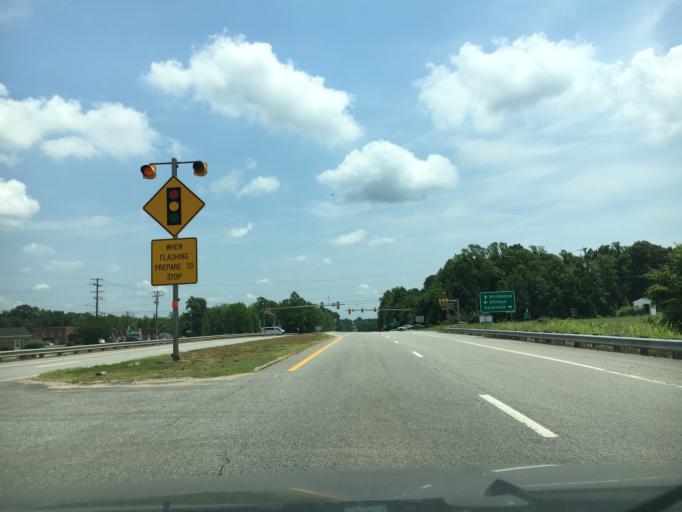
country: US
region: Virginia
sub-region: Buckingham County
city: Buckingham
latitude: 37.5298
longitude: -78.4937
